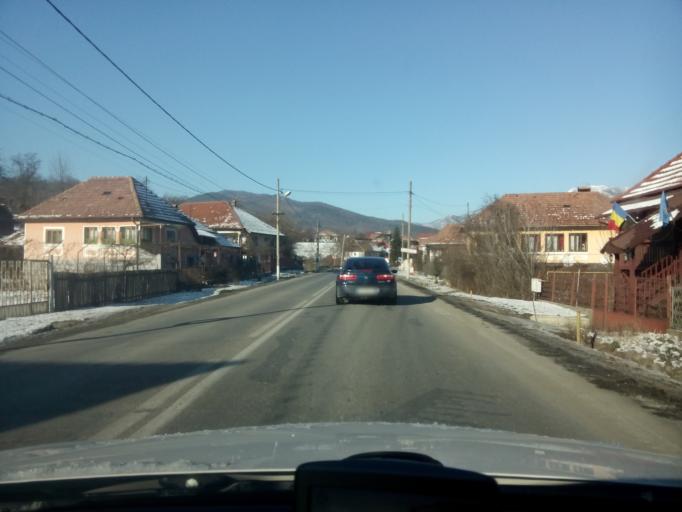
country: RO
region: Valcea
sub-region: Oras Calimanesti
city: Calimanesti
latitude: 45.2259
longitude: 24.3410
